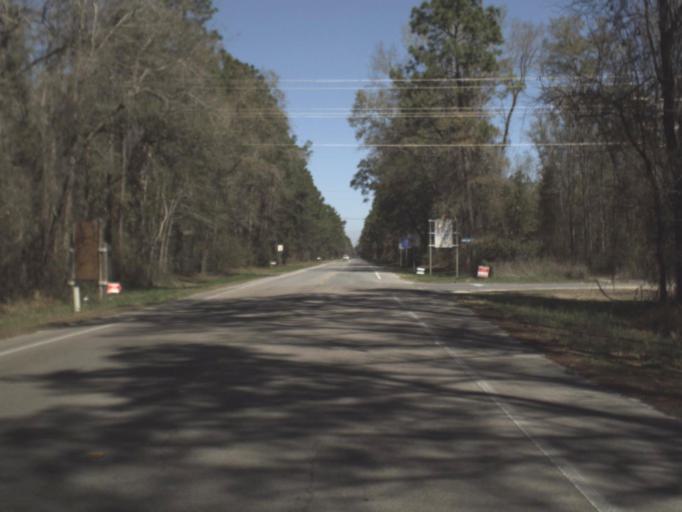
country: US
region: Florida
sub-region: Leon County
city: Woodville
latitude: 30.3028
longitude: -84.3119
